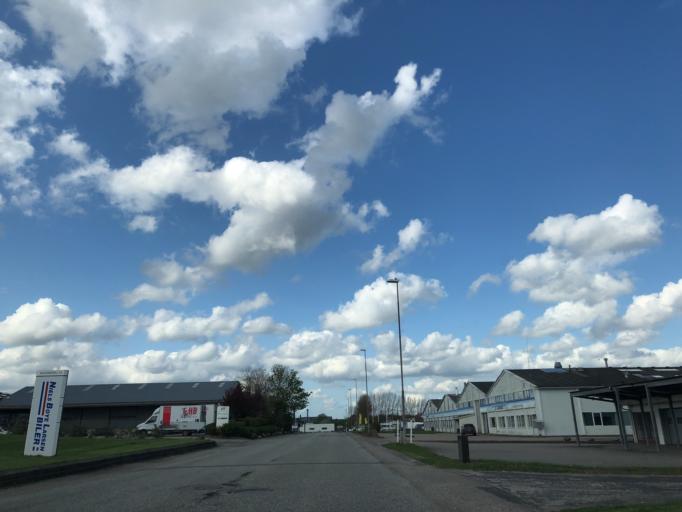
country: DK
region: Zealand
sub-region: Ringsted Kommune
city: Ringsted
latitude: 55.4258
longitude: 11.7899
